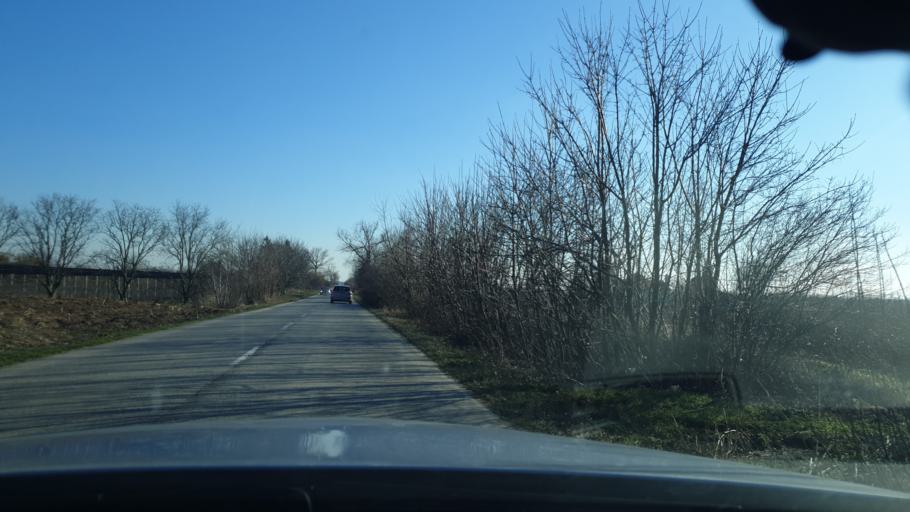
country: RS
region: Autonomna Pokrajina Vojvodina
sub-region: Sremski Okrug
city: Ruma
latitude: 45.0405
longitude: 19.8055
